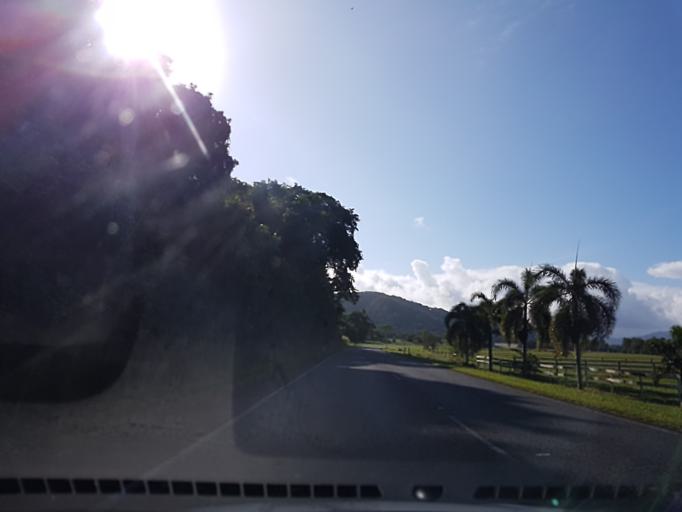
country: AU
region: Queensland
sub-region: Cairns
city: Port Douglas
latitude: -16.3570
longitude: 145.4095
